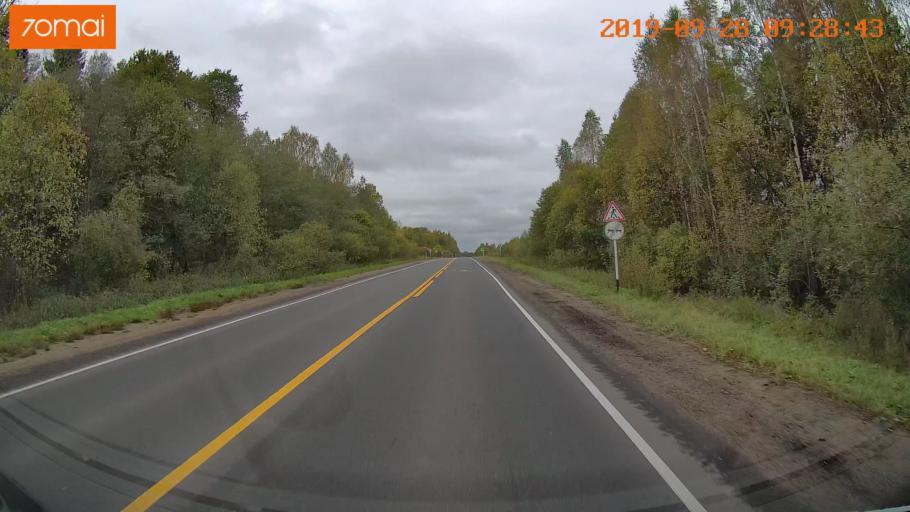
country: RU
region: Jaroslavl
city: Dubki
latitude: 57.2205
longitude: 40.2611
